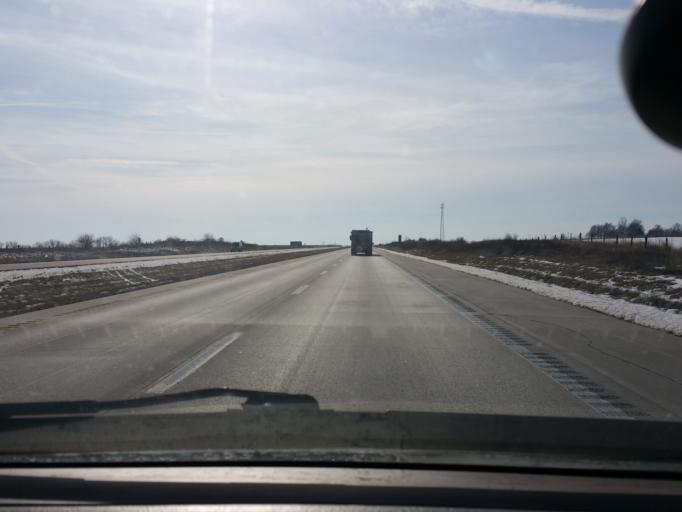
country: US
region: Missouri
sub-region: Clinton County
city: Lathrop
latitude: 39.5835
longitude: -94.2586
